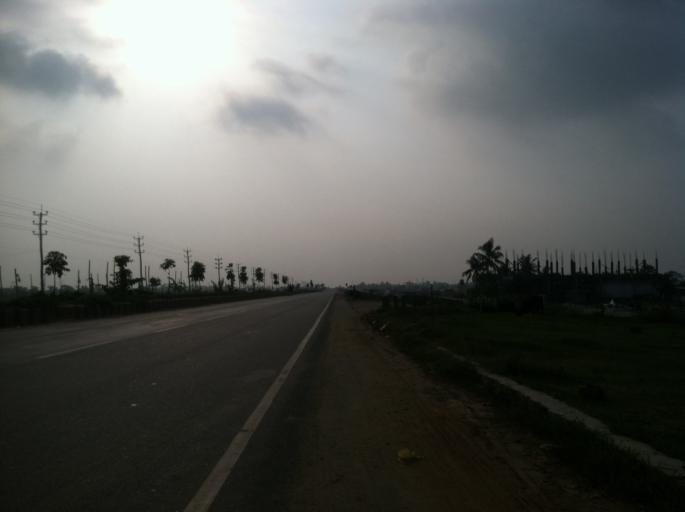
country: BD
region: Dhaka
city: Tungi
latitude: 23.8373
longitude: 90.4811
